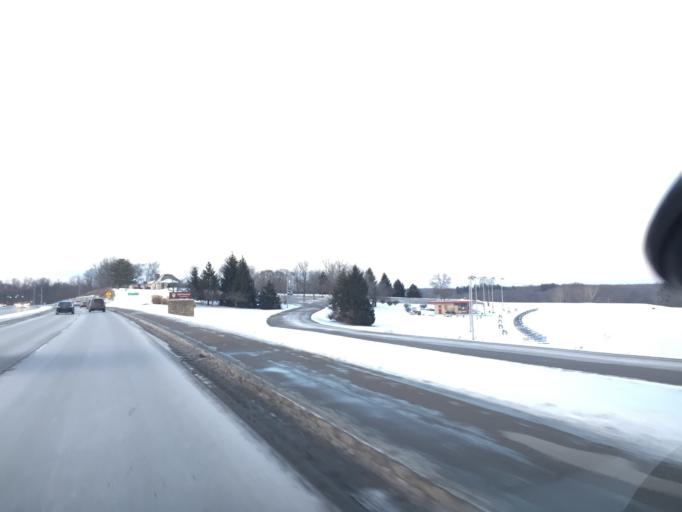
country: US
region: Indiana
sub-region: Monroe County
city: Bloomington
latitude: 39.1765
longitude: -86.5049
